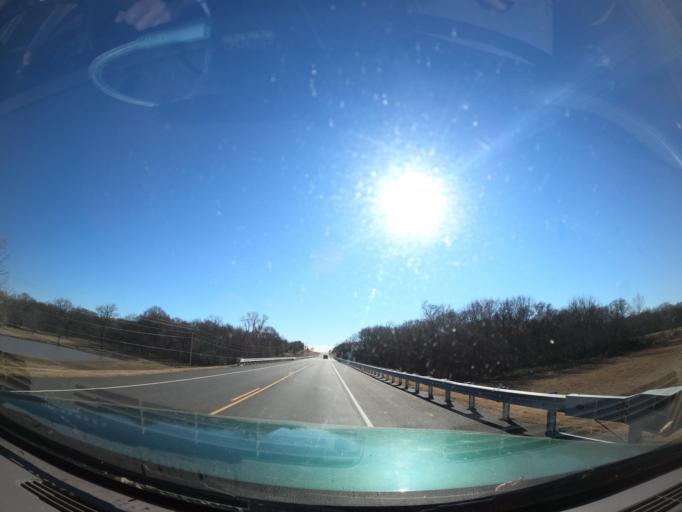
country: US
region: Oklahoma
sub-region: Muskogee County
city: Haskell
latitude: 35.8439
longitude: -95.6776
